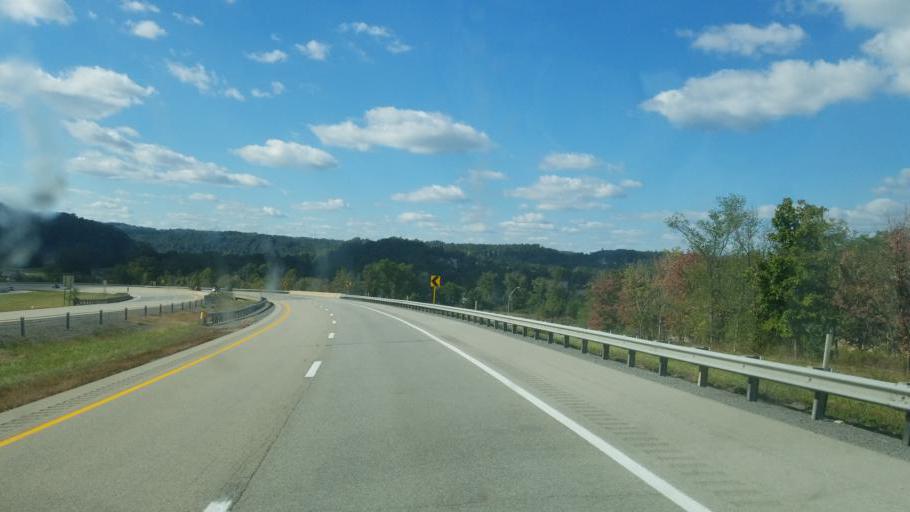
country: US
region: West Virginia
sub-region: Monongalia County
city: Cheat Lake
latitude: 39.6710
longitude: -79.8494
